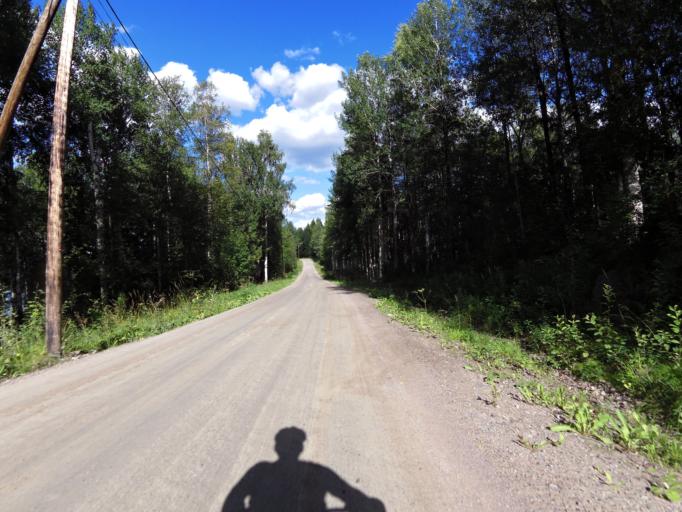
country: SE
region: Dalarna
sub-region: Faluns Kommun
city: Svardsjo
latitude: 60.6969
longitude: 15.8930
